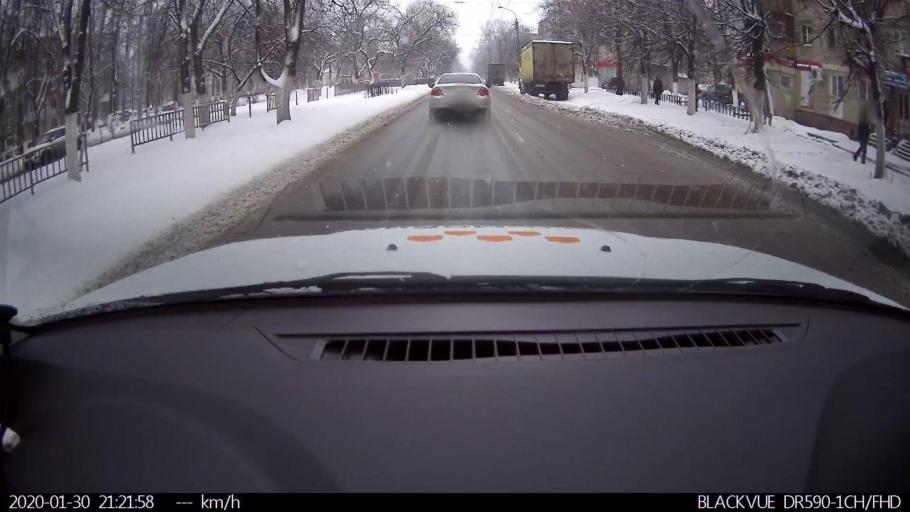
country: RU
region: Nizjnij Novgorod
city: Burevestnik
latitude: 56.2346
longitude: 43.8578
